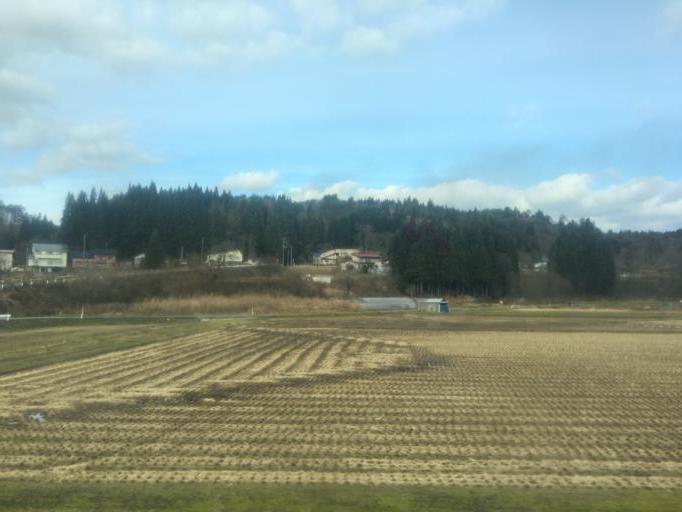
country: JP
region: Akita
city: Takanosu
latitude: 40.2244
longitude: 140.3335
